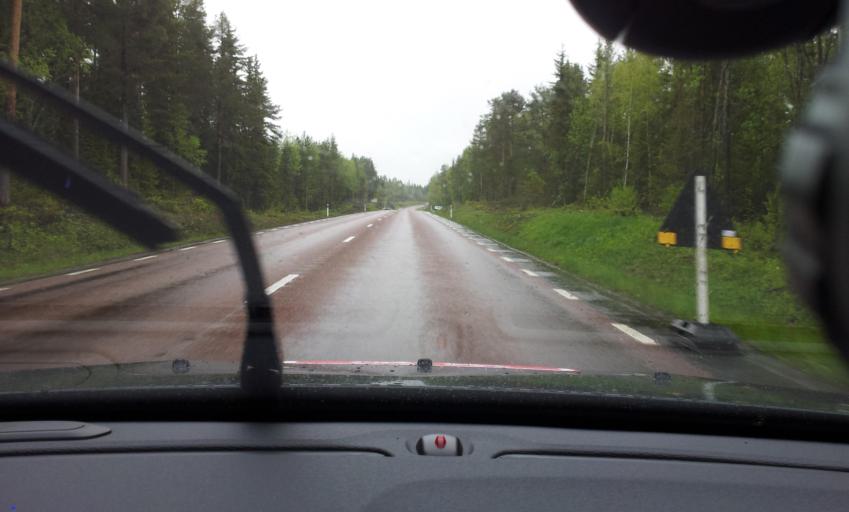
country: SE
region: Jaemtland
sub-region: Bergs Kommun
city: Hoverberg
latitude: 62.9442
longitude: 14.5434
